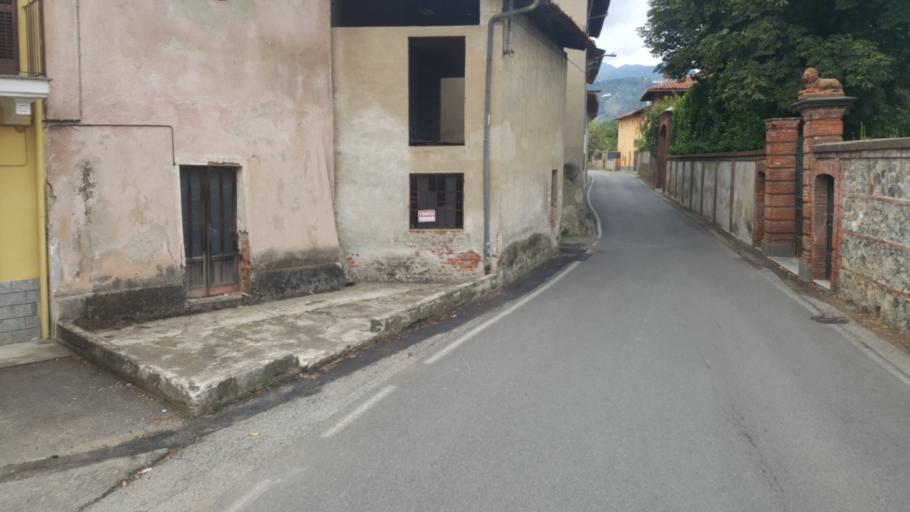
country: IT
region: Piedmont
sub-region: Provincia di Torino
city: San Ponso
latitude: 45.3507
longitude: 7.6692
